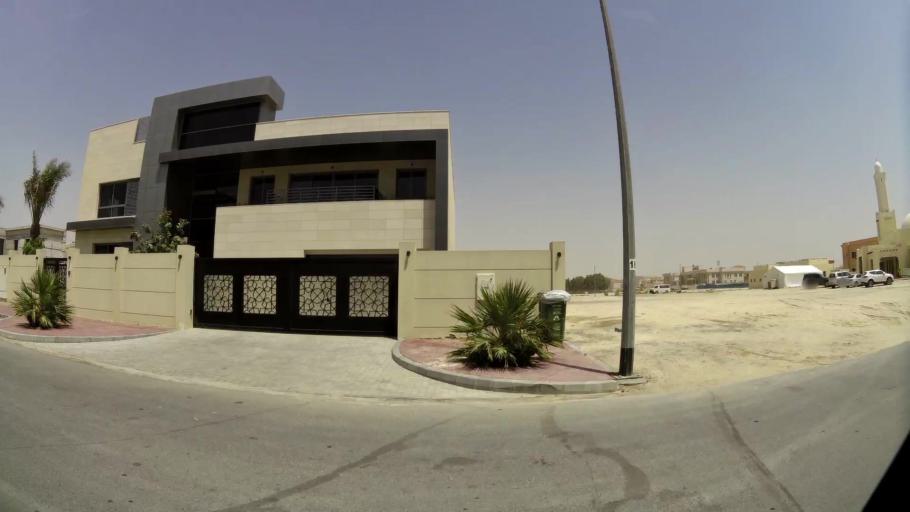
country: AE
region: Dubai
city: Dubai
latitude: 25.1373
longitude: 55.2036
